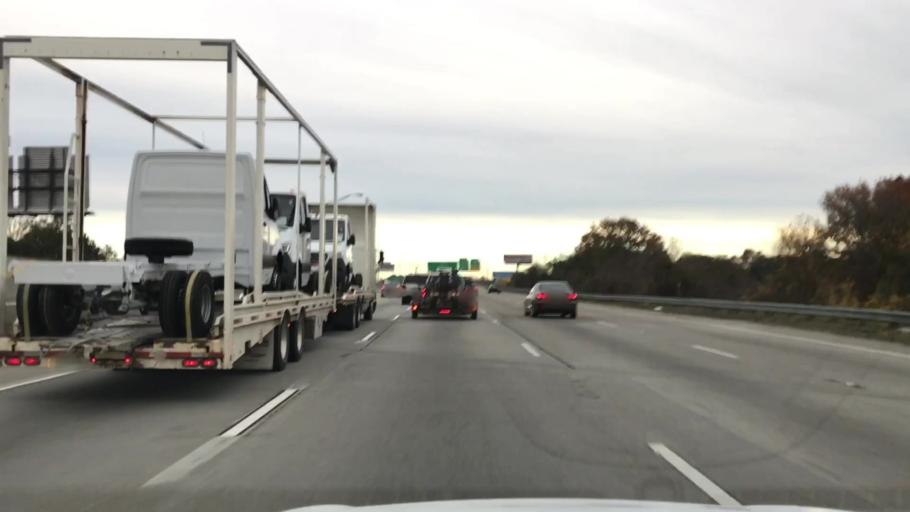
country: US
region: South Carolina
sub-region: Berkeley County
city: Hanahan
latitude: 32.8887
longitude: -80.0191
